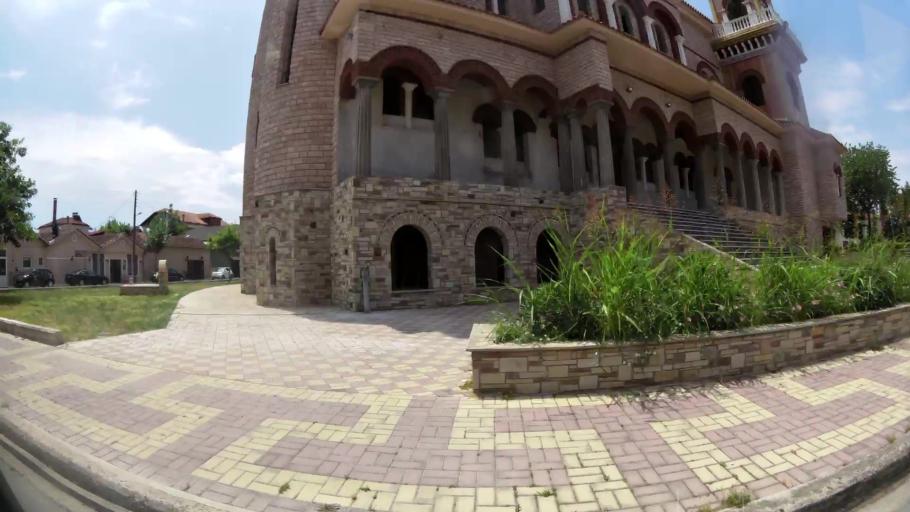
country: GR
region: Central Macedonia
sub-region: Nomos Pierias
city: Peristasi
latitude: 40.2734
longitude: 22.5408
